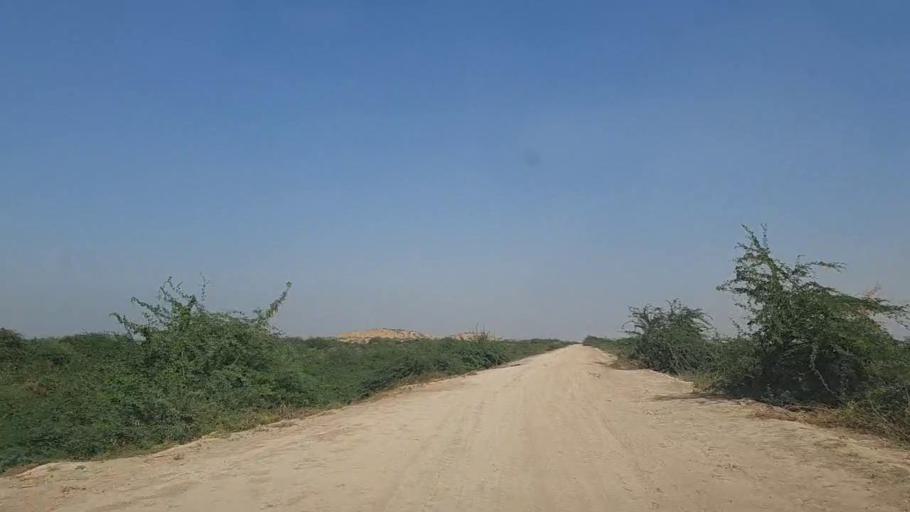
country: PK
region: Sindh
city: Daro Mehar
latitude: 24.8617
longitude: 68.0398
